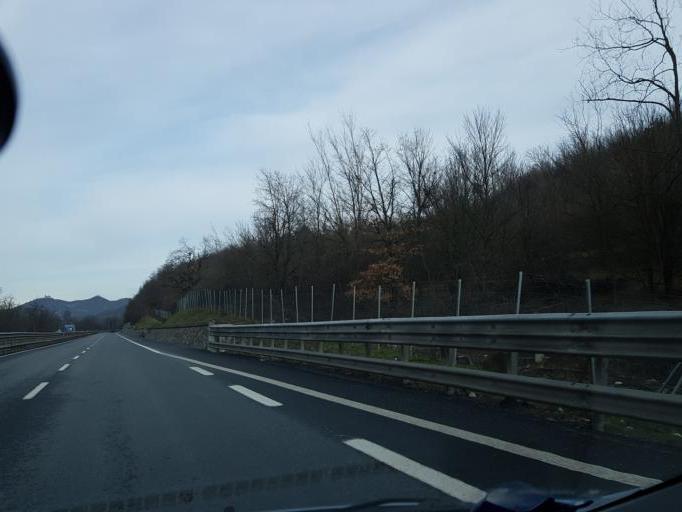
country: IT
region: Piedmont
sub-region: Provincia di Alessandria
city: Arquata Scrivia
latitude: 44.6772
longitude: 8.9050
